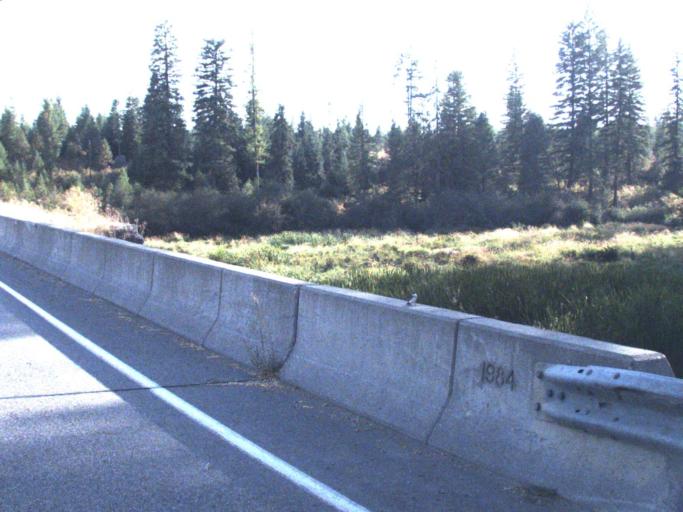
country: US
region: Washington
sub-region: Spokane County
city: Deer Park
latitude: 47.9972
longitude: -117.3496
